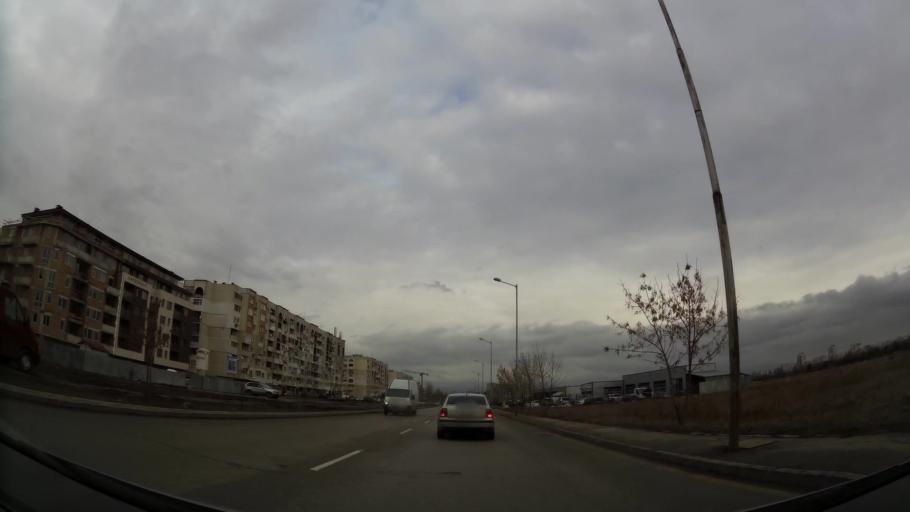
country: BG
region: Sofia-Capital
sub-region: Stolichna Obshtina
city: Sofia
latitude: 42.7356
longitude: 23.2712
